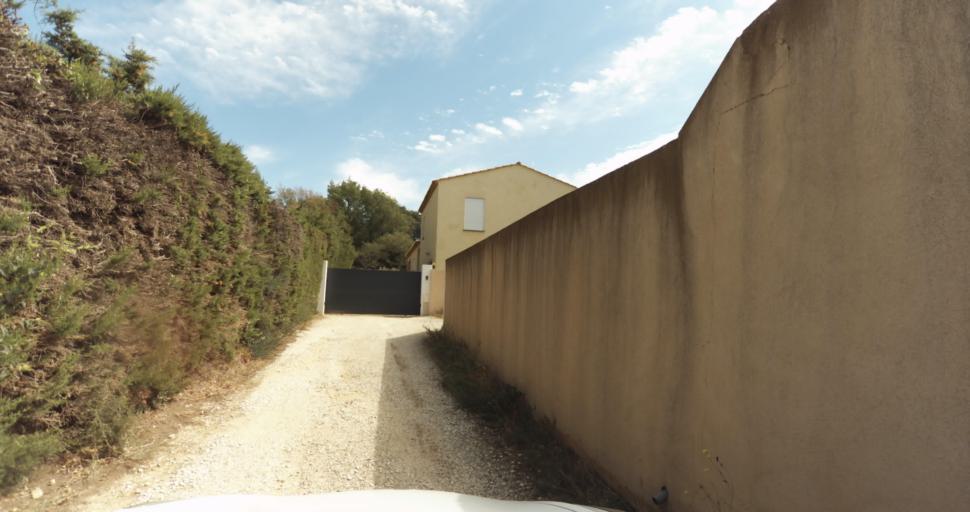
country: FR
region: Provence-Alpes-Cote d'Azur
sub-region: Departement des Bouches-du-Rhone
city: Miramas
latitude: 43.5782
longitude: 5.0222
